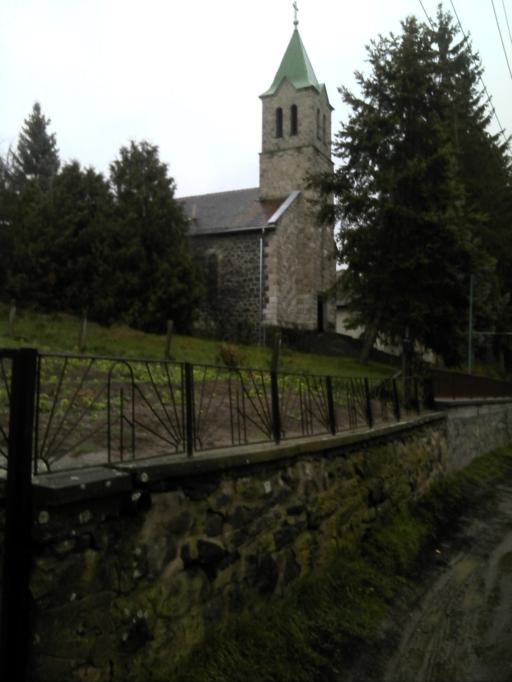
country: HU
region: Nograd
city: Bujak
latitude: 47.9405
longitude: 19.5803
